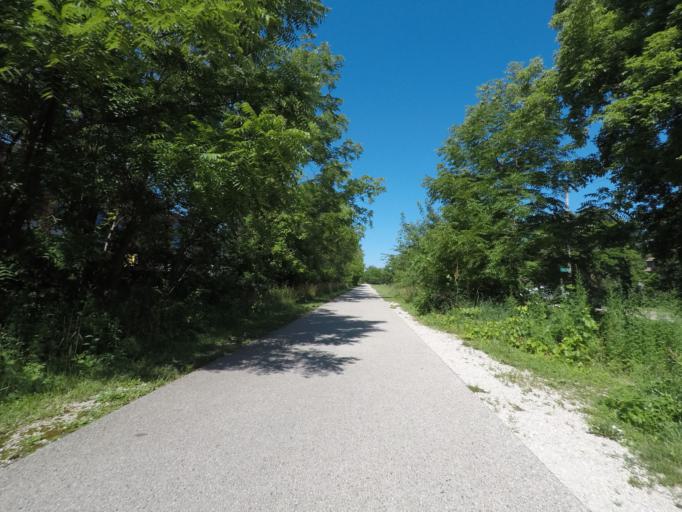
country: US
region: Wisconsin
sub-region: Milwaukee County
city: West Milwaukee
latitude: 43.0242
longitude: -87.9883
